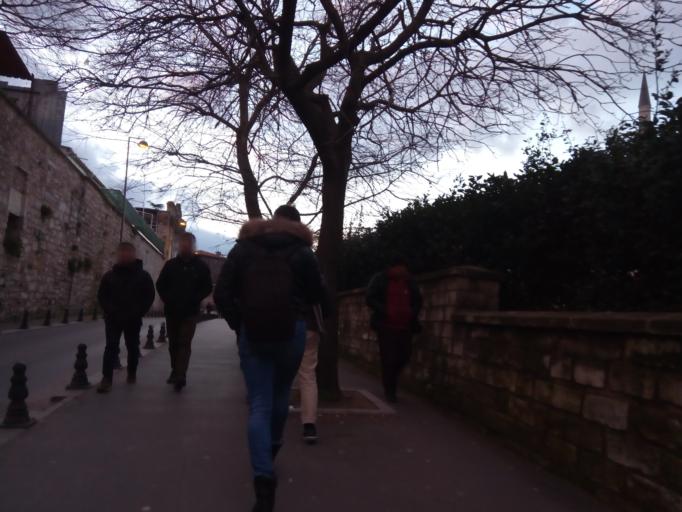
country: TR
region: Istanbul
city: Eminoenue
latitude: 41.0150
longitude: 28.9649
